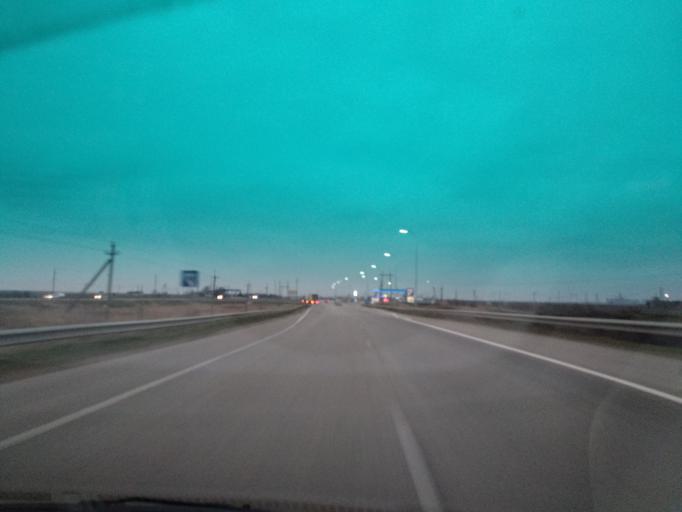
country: RU
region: Adygeya
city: Adygeysk
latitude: 44.8694
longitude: 39.1866
